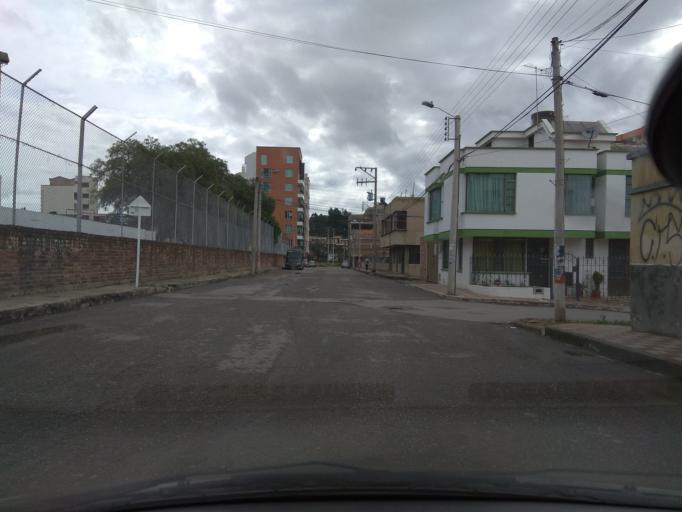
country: CO
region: Boyaca
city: Duitama
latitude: 5.8328
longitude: -73.0347
